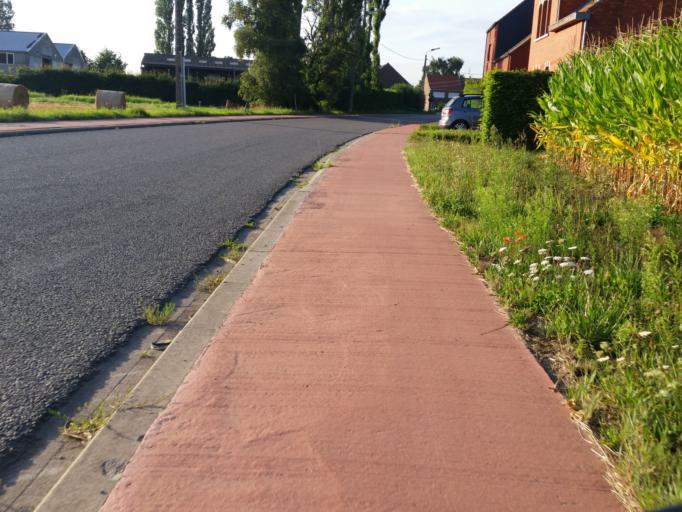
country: BE
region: Flanders
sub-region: Provincie Vlaams-Brabant
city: Zemst
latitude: 50.9724
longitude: 4.4360
